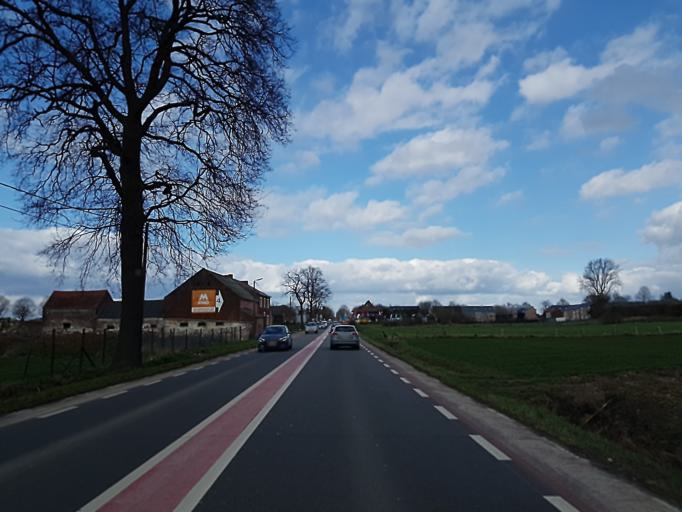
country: BE
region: Wallonia
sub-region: Province du Brabant Wallon
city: Perwez
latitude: 50.6342
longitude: 4.7770
